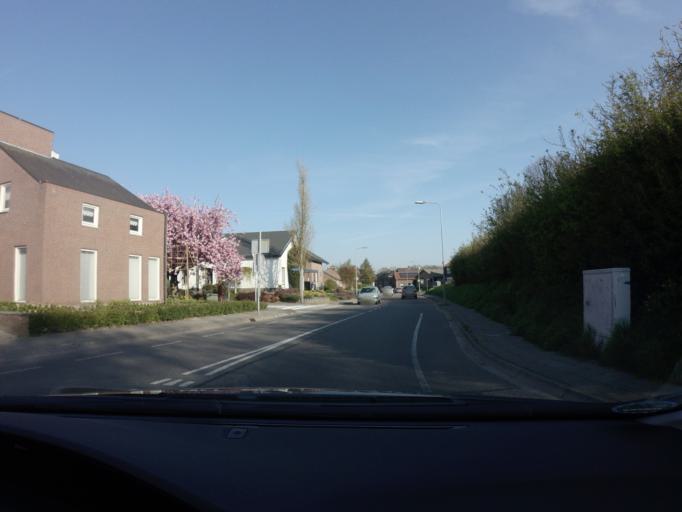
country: NL
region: Limburg
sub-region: Gemeente Stein
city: Elsloo
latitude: 50.9262
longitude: 5.7602
